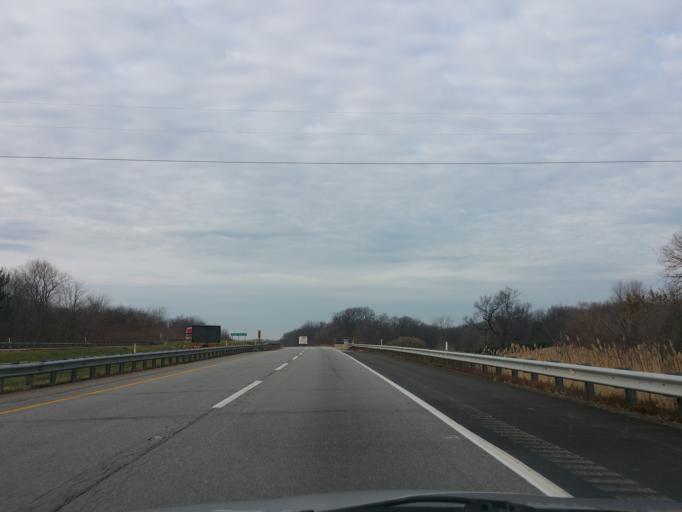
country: US
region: Indiana
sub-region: LaPorte County
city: LaPorte
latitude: 41.6748
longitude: -86.6980
